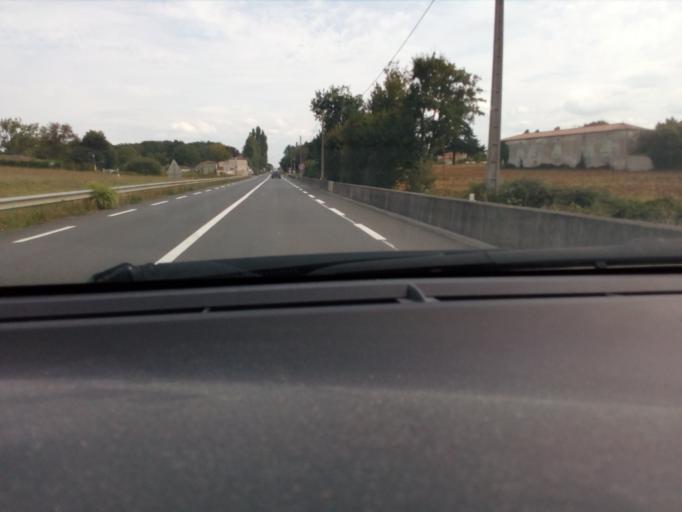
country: FR
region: Poitou-Charentes
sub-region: Departement de la Charente
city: Fleac
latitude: 45.6755
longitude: 0.0900
